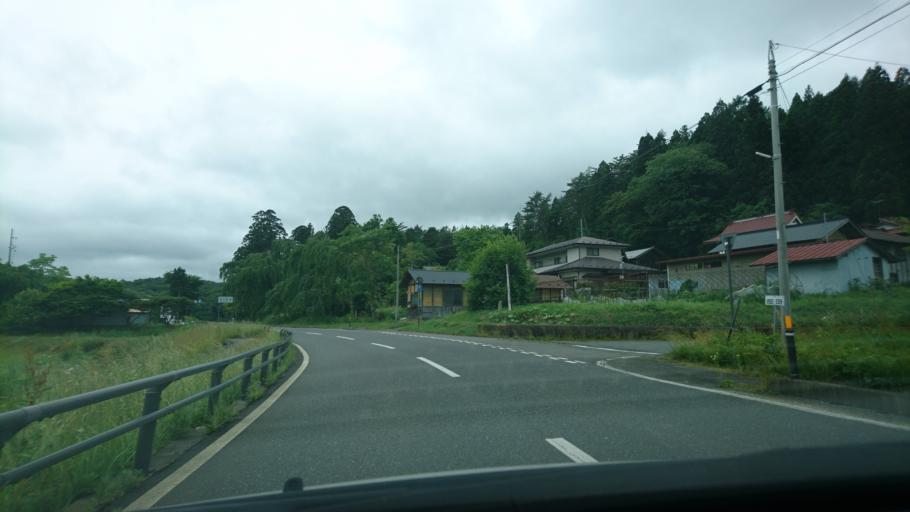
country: JP
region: Iwate
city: Ichinoseki
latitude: 38.9691
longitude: 141.0607
